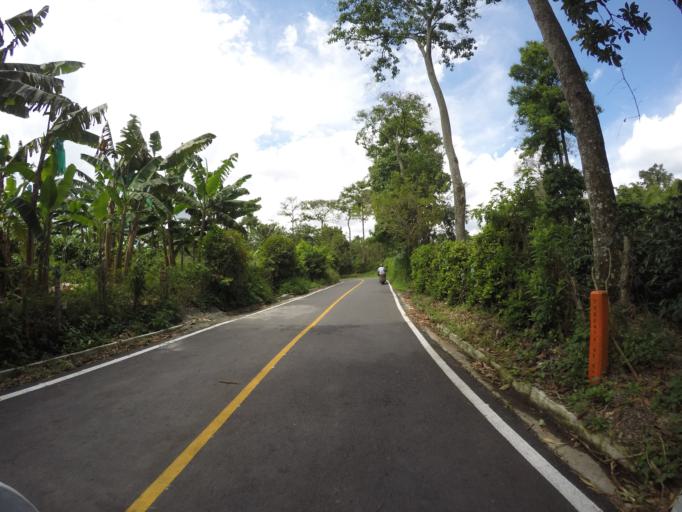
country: CO
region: Quindio
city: Quimbaya
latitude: 4.6126
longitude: -75.7619
